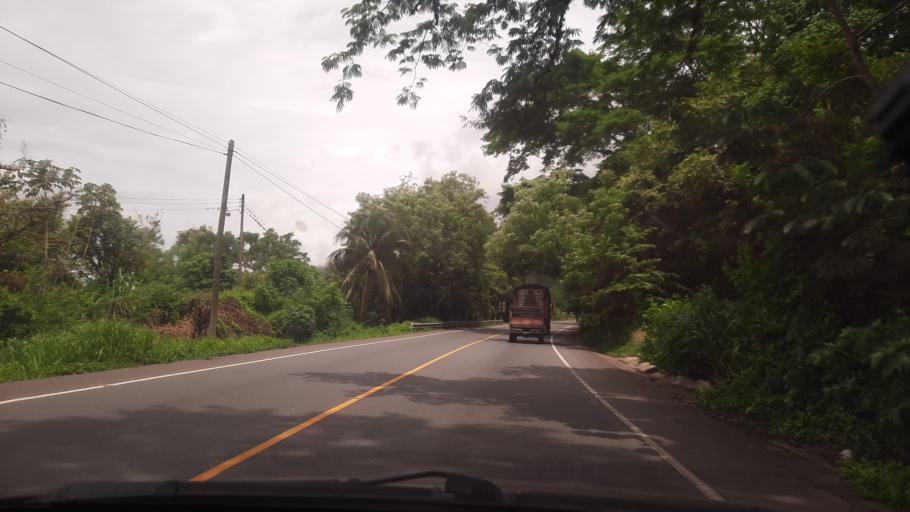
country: GT
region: Zacapa
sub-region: Municipio de Zacapa
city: Gualan
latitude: 15.1970
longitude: -89.2665
